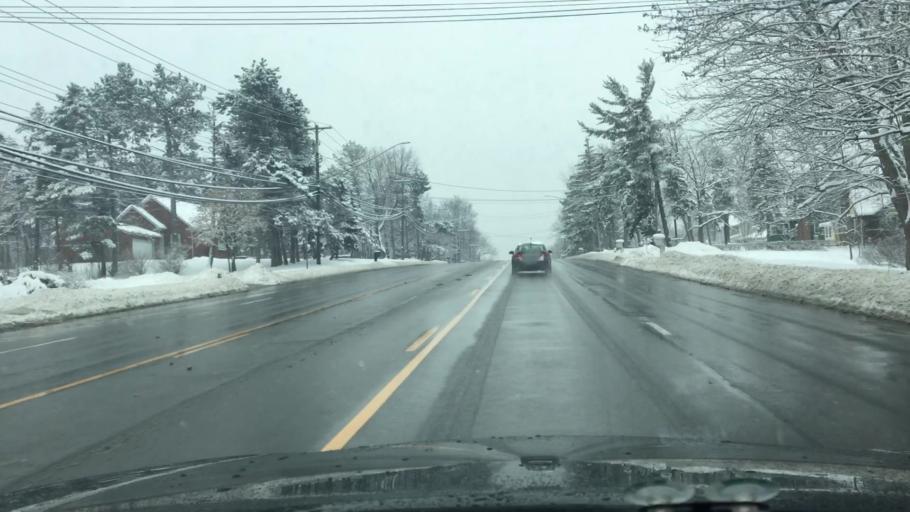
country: US
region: New York
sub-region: Erie County
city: Orchard Park
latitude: 42.8104
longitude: -78.7519
